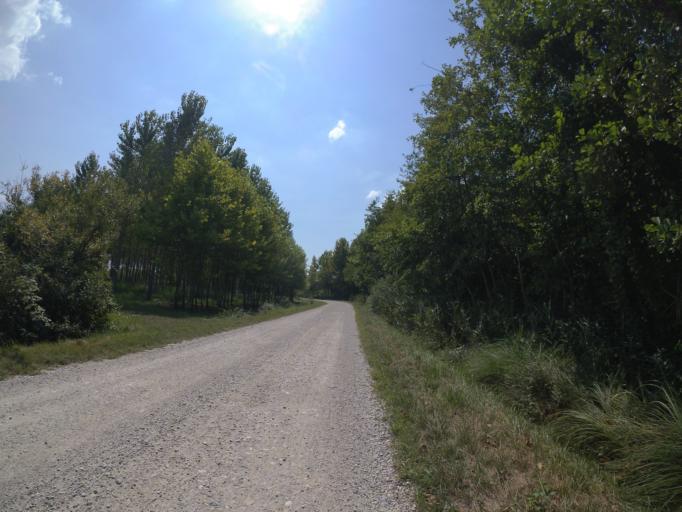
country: IT
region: Friuli Venezia Giulia
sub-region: Provincia di Udine
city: Bertiolo
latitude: 45.9195
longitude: 13.0625
